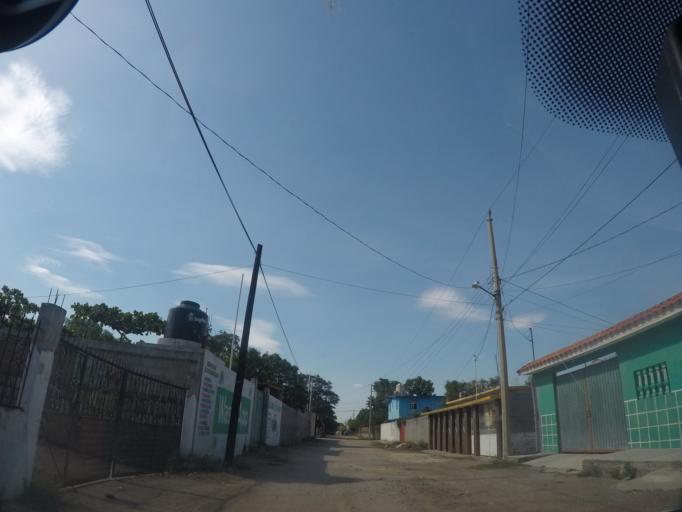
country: MX
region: Oaxaca
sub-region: Salina Cruz
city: Salina Cruz
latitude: 16.2153
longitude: -95.1995
